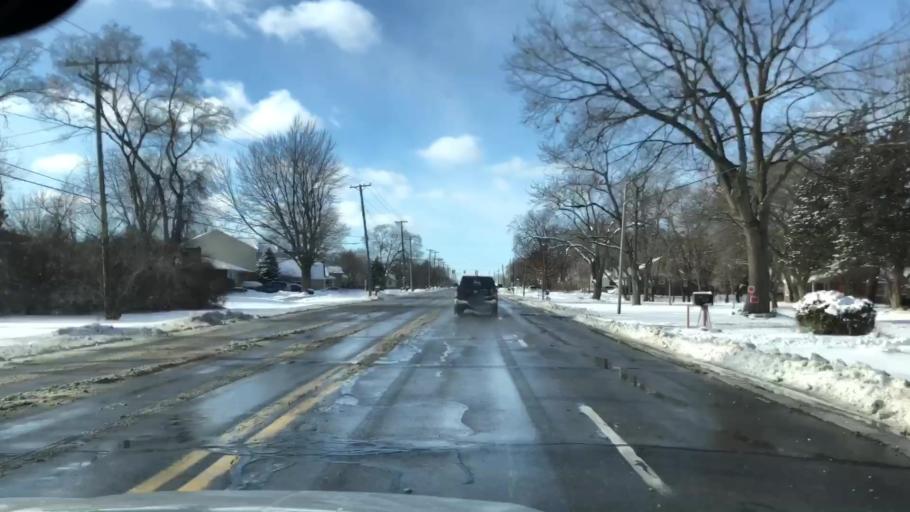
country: US
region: Michigan
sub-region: Wayne County
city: Westland
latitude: 42.3688
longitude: -83.4139
